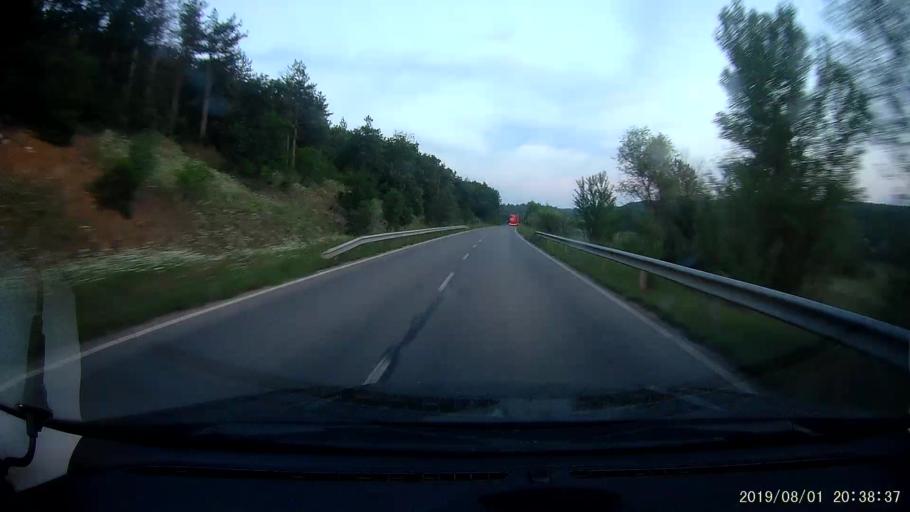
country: BG
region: Yambol
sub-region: Obshtina Elkhovo
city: Elkhovo
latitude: 42.0220
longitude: 26.6019
